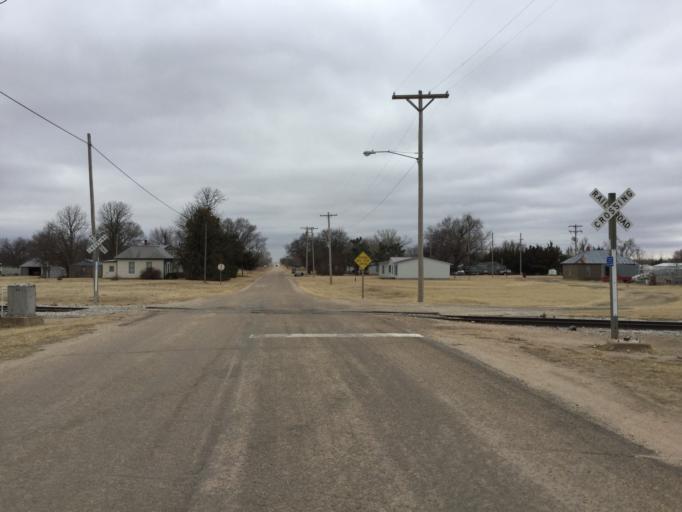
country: US
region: Kansas
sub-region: Barton County
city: Ellinwood
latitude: 38.2770
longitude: -98.4159
